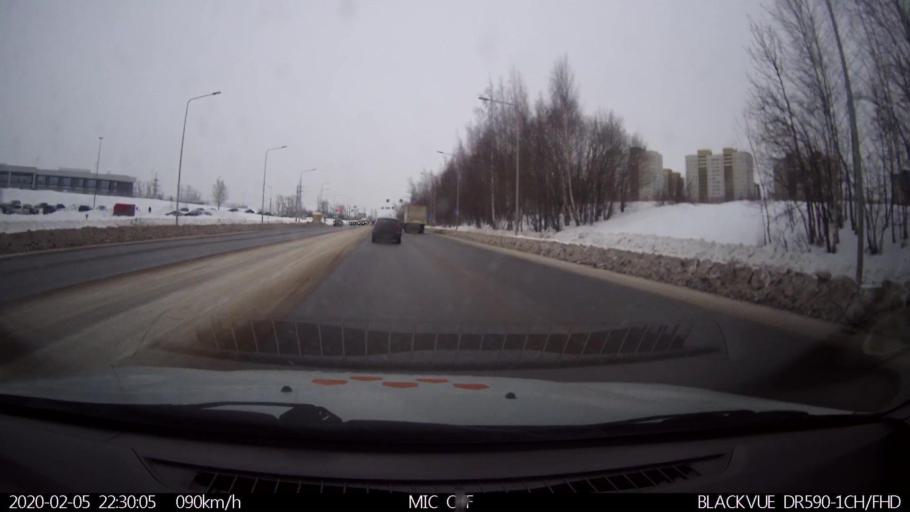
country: RU
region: Nizjnij Novgorod
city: Imeni Stepana Razina
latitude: 54.7449
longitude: 44.1544
